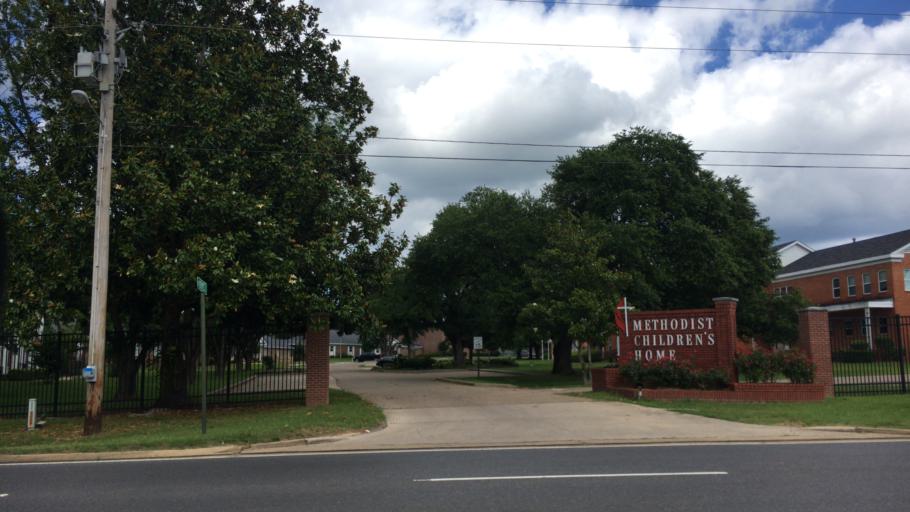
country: US
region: Louisiana
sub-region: Lincoln Parish
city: Ruston
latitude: 32.5188
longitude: -92.6387
